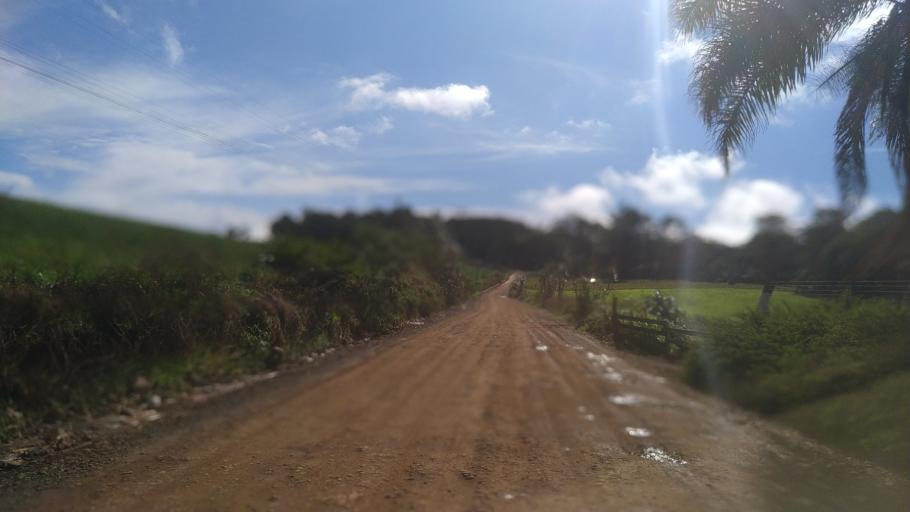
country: BR
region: Santa Catarina
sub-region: Chapeco
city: Chapeco
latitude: -27.1450
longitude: -52.5944
